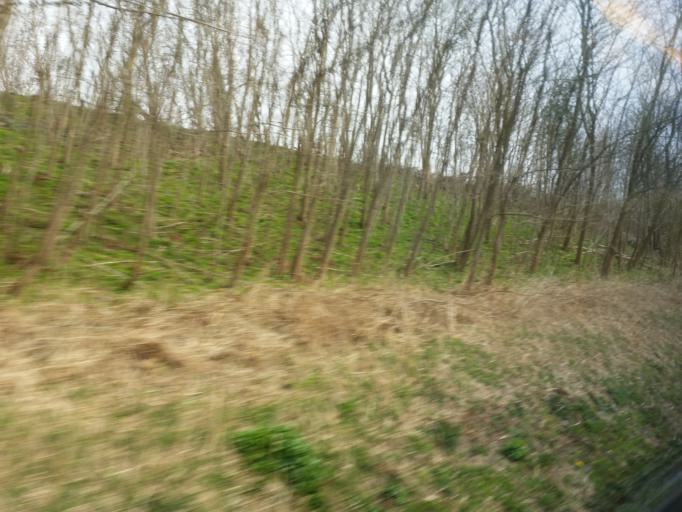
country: BE
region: Flanders
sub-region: Provincie Oost-Vlaanderen
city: Sint-Lievens-Houtem
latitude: 50.9514
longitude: 3.9100
